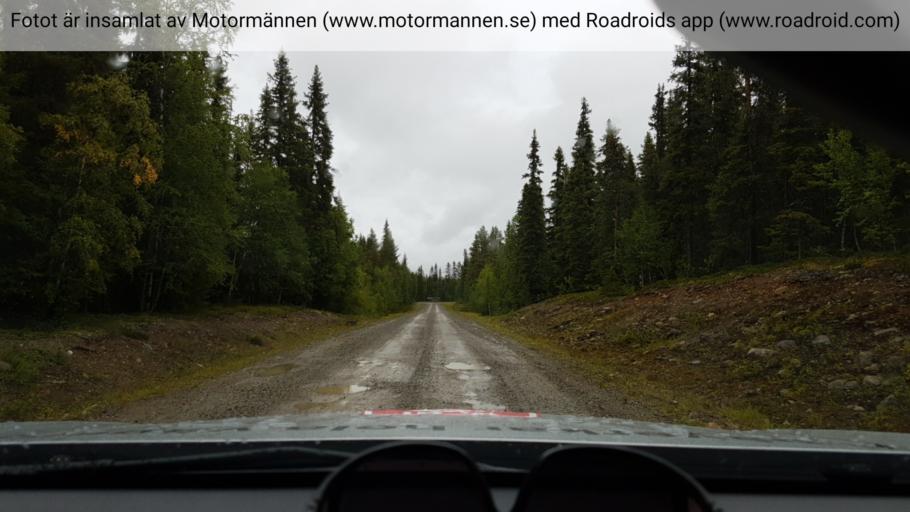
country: SE
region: Vaesterbotten
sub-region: Lycksele Kommun
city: Soderfors
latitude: 64.7891
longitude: 17.6443
